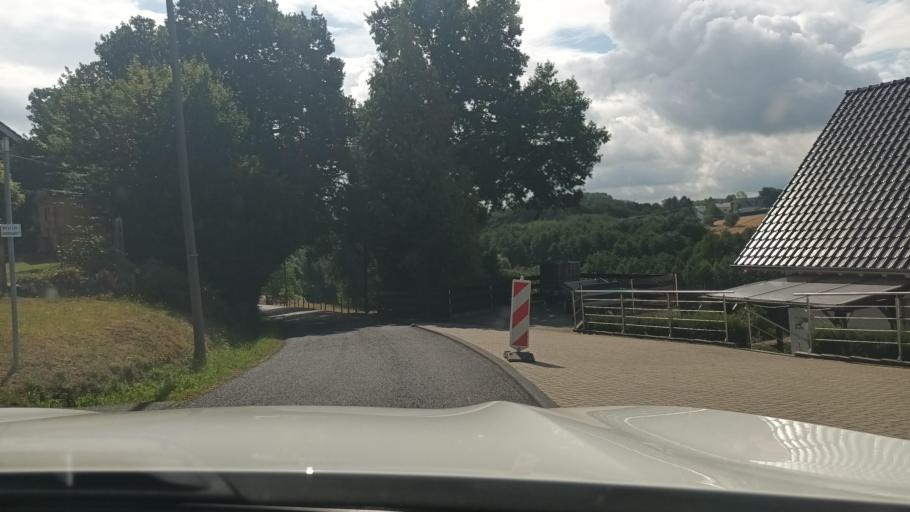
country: DE
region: North Rhine-Westphalia
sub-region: Regierungsbezirk Koln
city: Hennef
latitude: 50.7372
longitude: 7.3538
